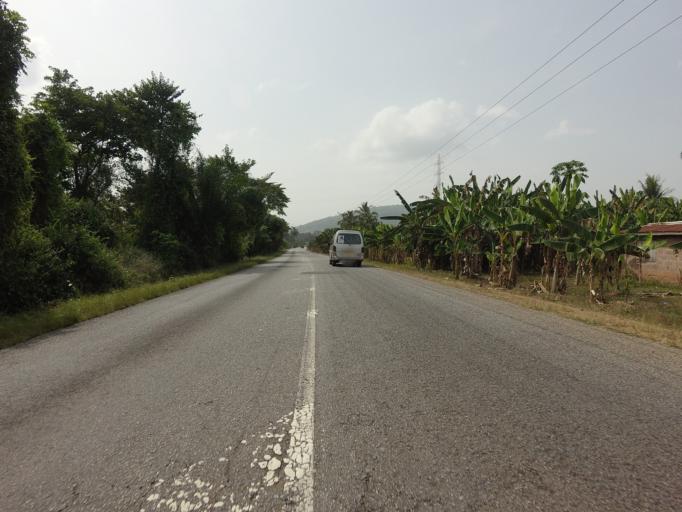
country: GH
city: Akropong
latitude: 6.2979
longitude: 0.1344
